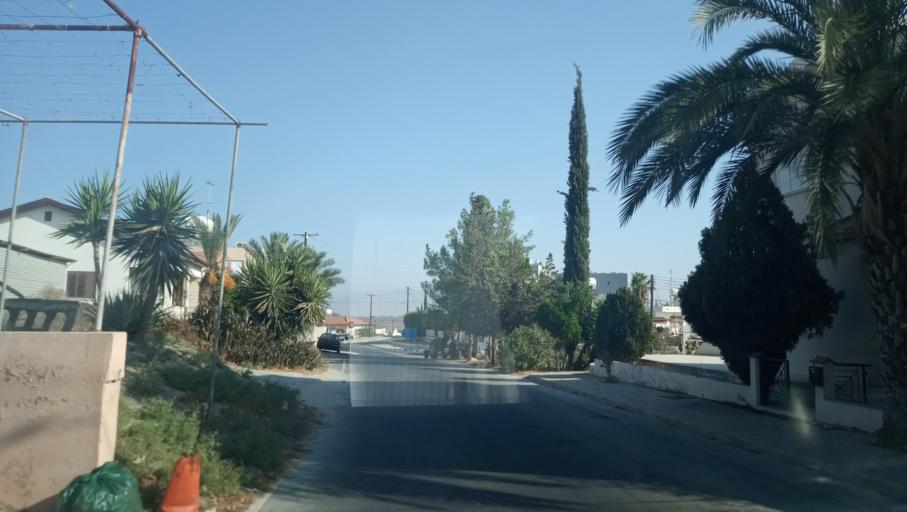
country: CY
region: Lefkosia
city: Geri
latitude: 35.1106
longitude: 33.4228
